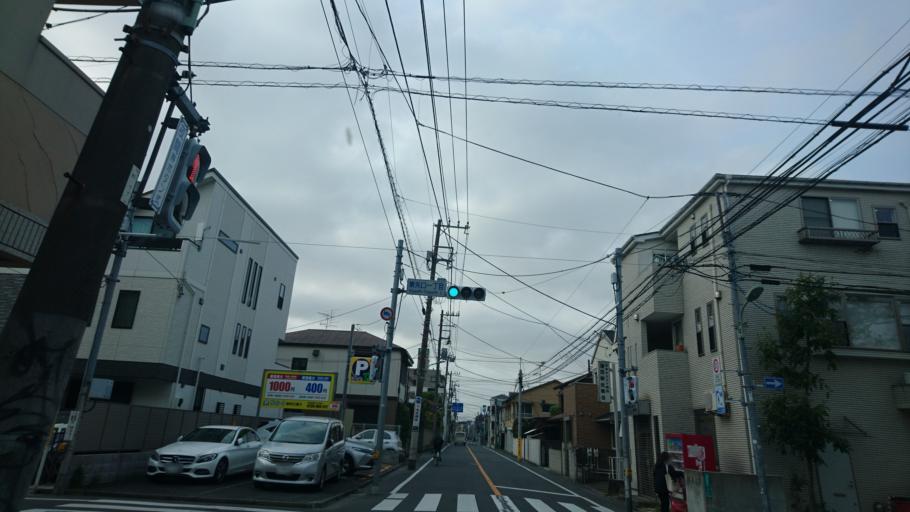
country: JP
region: Kanagawa
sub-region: Kawasaki-shi
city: Kawasaki
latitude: 35.5656
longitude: 139.7044
